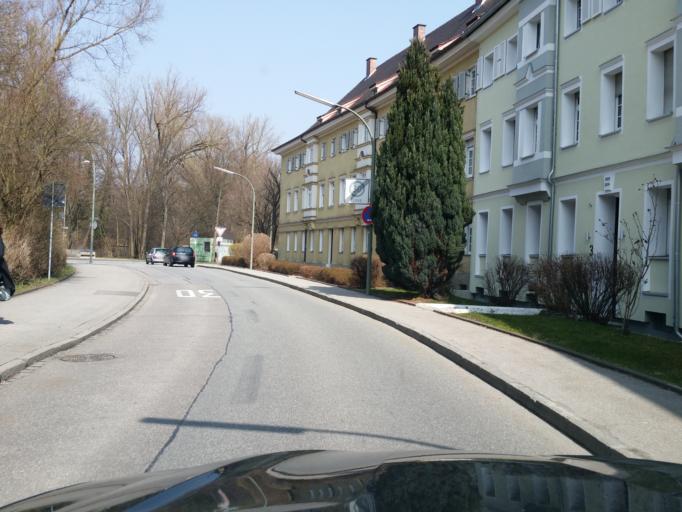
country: DE
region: Bavaria
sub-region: Lower Bavaria
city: Landshut
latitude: 48.5341
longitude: 12.1391
